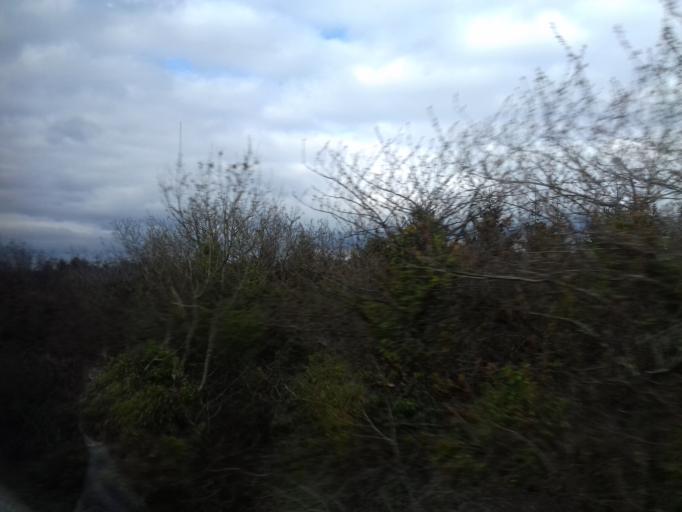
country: IE
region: Leinster
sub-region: An Iarmhi
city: Castlepollard
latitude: 53.6409
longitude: -7.4203
